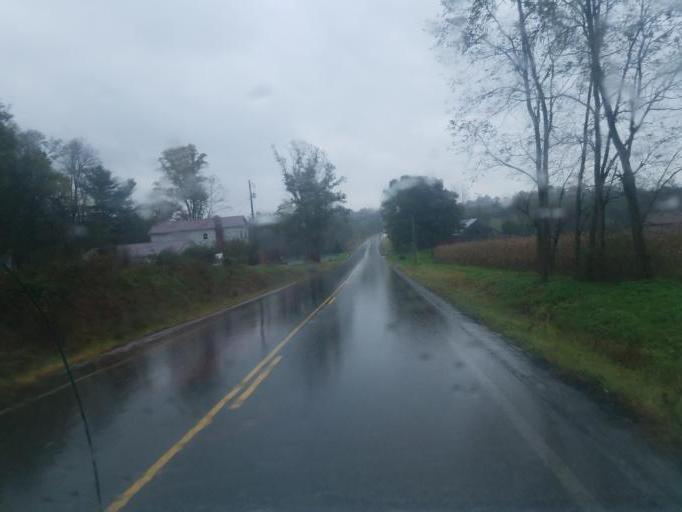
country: US
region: Ohio
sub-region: Licking County
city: Utica
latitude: 40.2461
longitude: -82.3189
